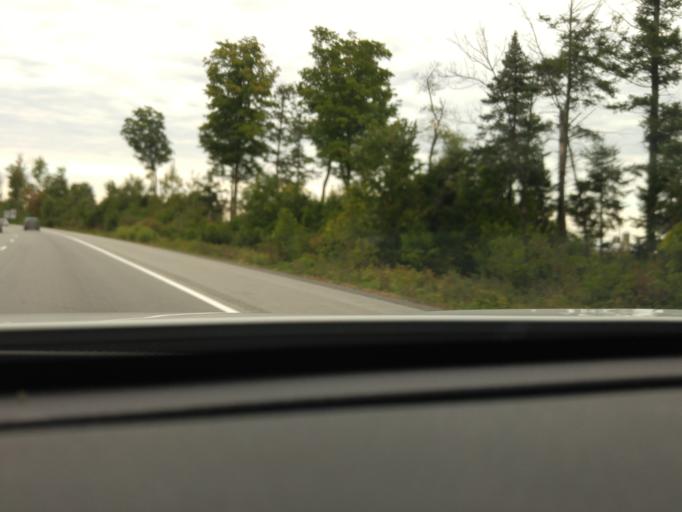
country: CA
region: Ontario
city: Arnprior
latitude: 45.4149
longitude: -76.3025
